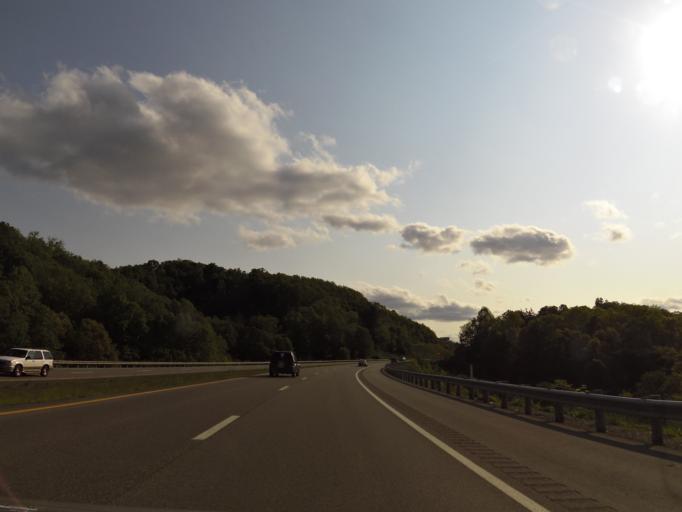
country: US
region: West Virginia
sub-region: Mercer County
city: Princeton
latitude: 37.3035
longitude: -81.1407
